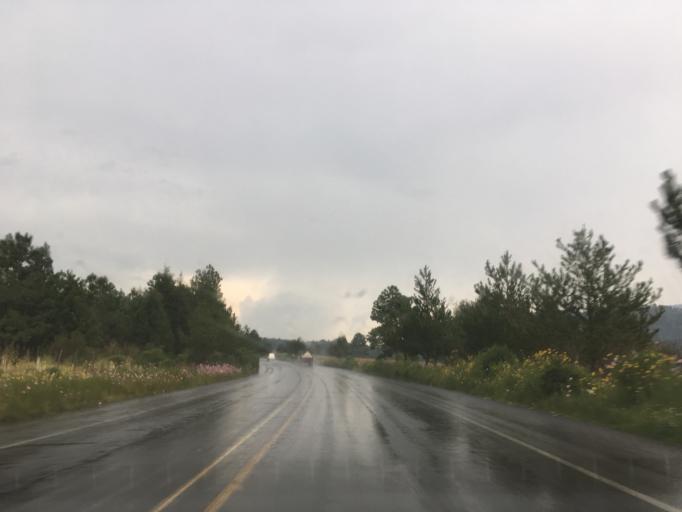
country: MX
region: Michoacan
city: Angahuan
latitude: 19.5408
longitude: -102.2044
